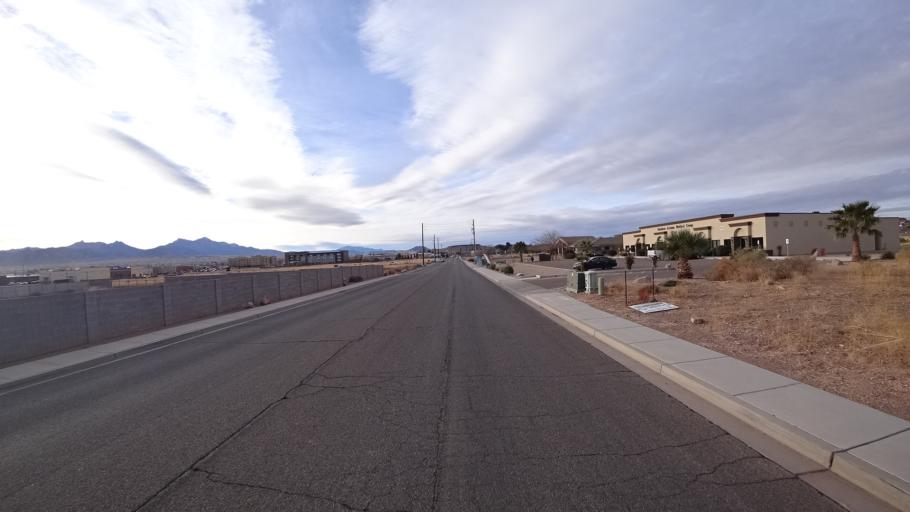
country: US
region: Arizona
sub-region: Mohave County
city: New Kingman-Butler
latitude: 35.2266
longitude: -114.0402
